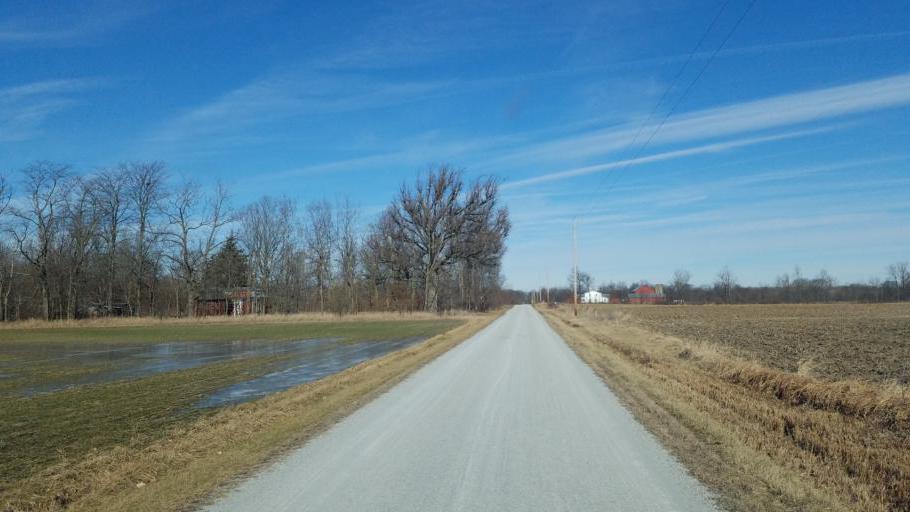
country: US
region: Ohio
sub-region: Hardin County
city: Kenton
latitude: 40.5871
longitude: -83.4216
